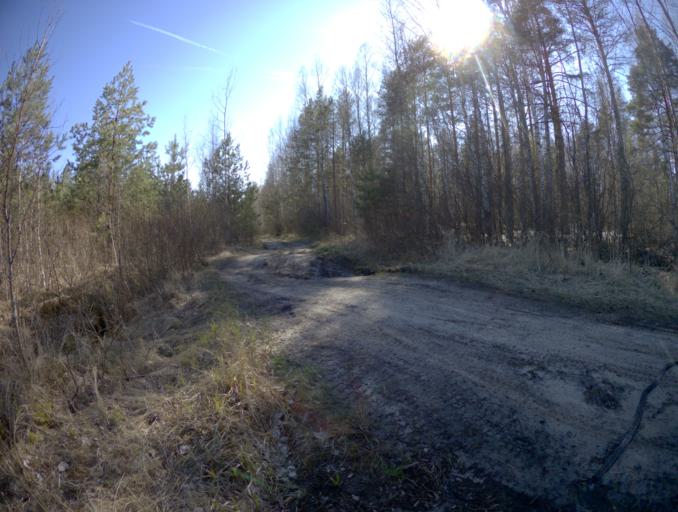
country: RU
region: Vladimir
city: Ivanishchi
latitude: 55.7522
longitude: 40.4080
